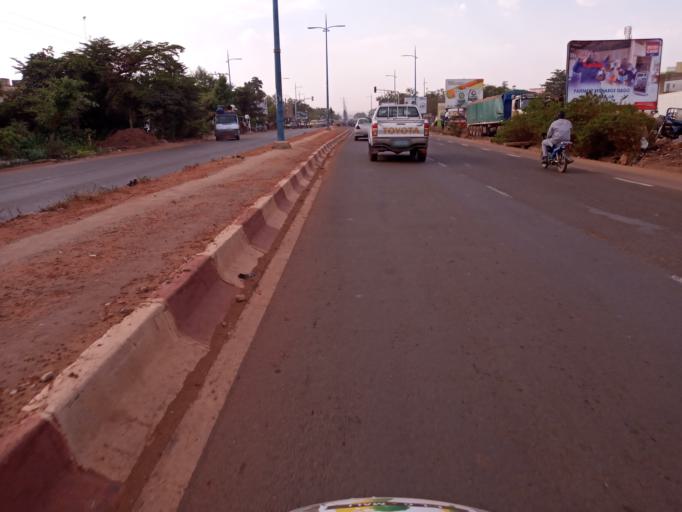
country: ML
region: Bamako
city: Bamako
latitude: 12.5884
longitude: -7.9482
